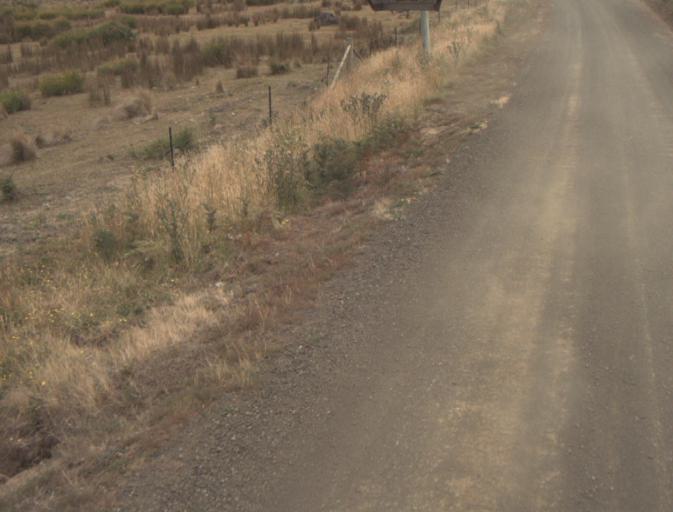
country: AU
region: Tasmania
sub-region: Northern Midlands
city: Evandale
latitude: -41.5233
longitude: 147.4563
